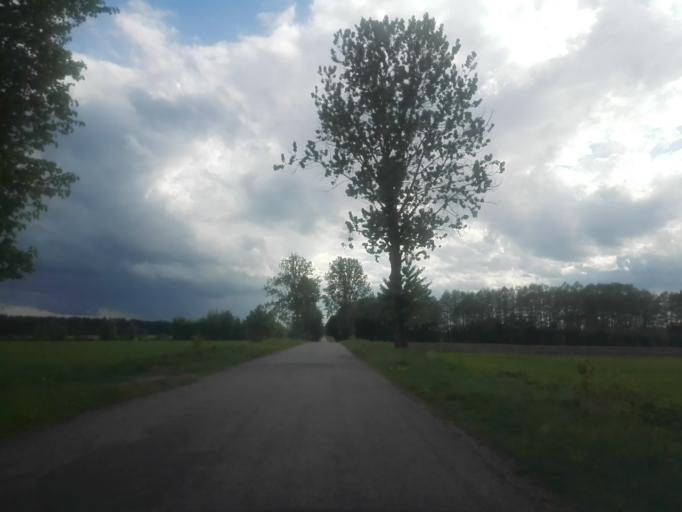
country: PL
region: Podlasie
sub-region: Powiat lomzynski
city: Wizna
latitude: 53.2147
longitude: 22.4097
